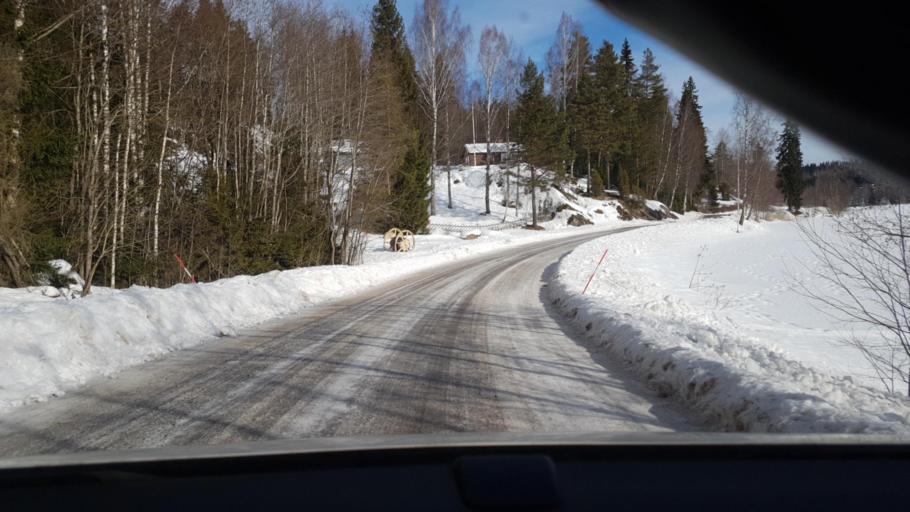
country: NO
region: Hedmark
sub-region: Eidskog
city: Skotterud
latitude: 59.8826
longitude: 11.9762
